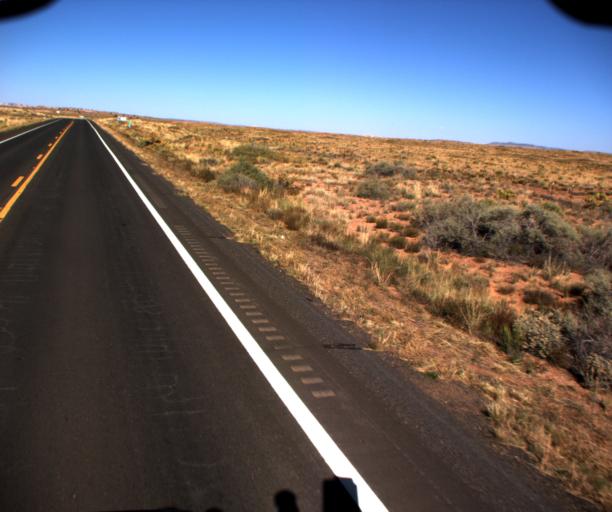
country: US
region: Arizona
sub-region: Coconino County
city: Tuba City
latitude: 36.2627
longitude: -111.0183
